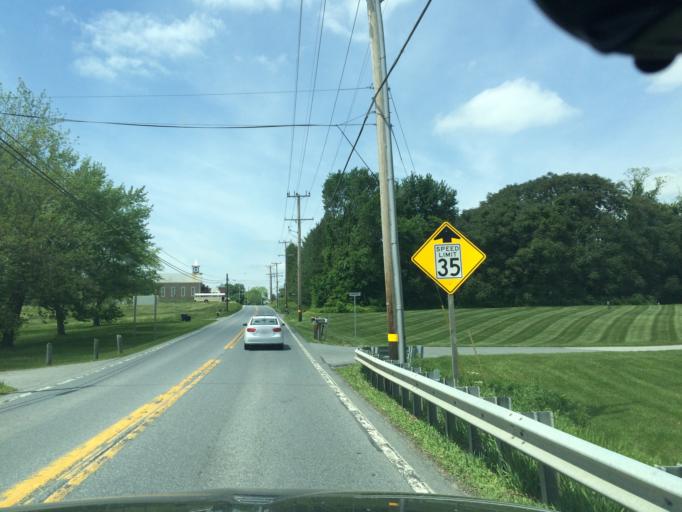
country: US
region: Maryland
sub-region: Carroll County
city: Eldersburg
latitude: 39.4576
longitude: -76.9296
